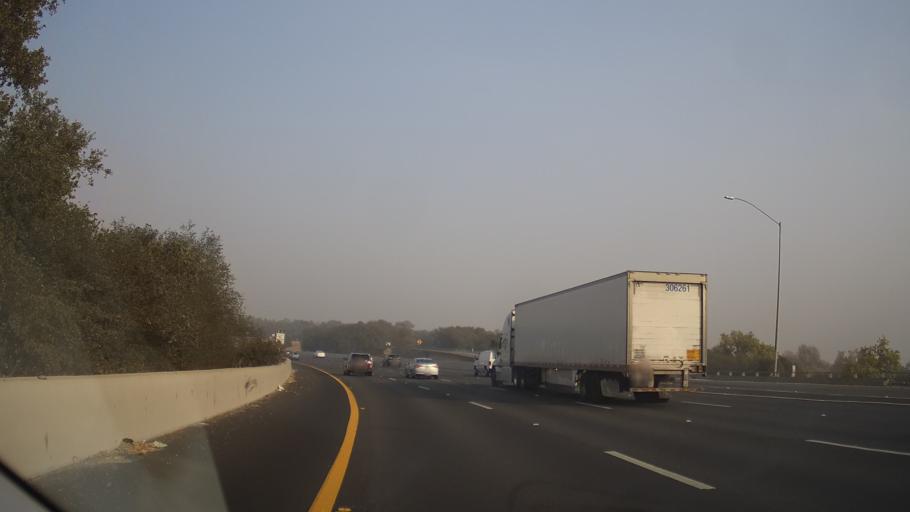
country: US
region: California
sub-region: Sacramento County
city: Arden-Arcade
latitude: 38.6375
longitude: -121.4030
